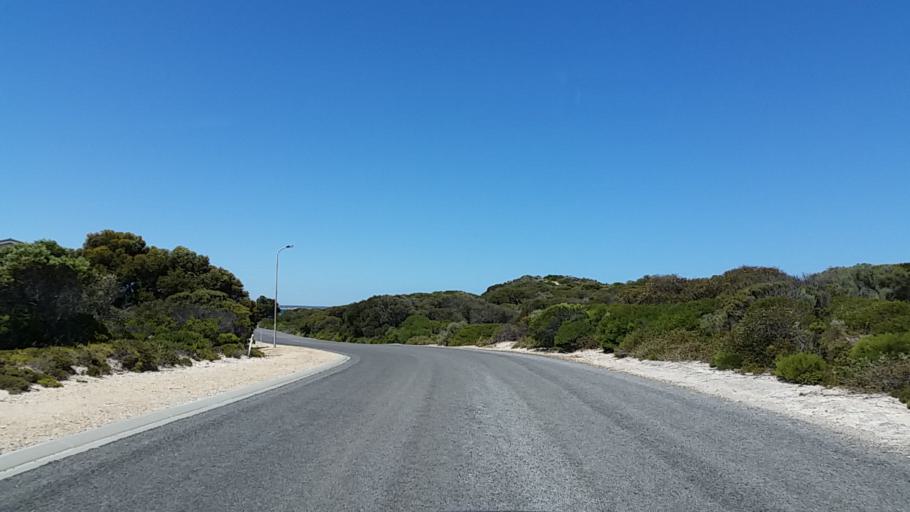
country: AU
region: South Australia
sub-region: Yorke Peninsula
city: Honiton
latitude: -35.2497
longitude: 136.9744
